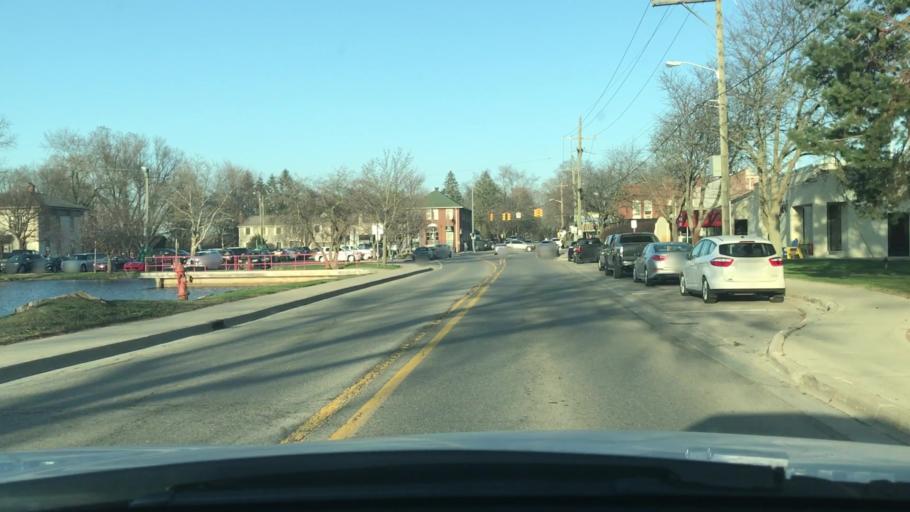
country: US
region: Michigan
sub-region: Oakland County
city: Clarkston
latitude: 42.7359
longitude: -83.4207
